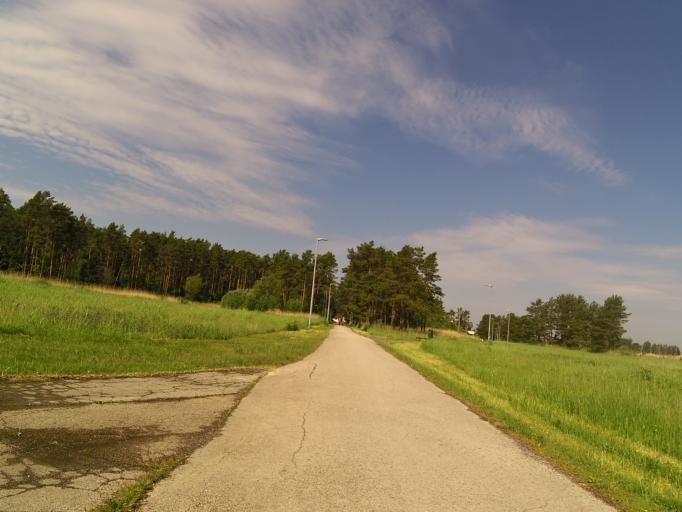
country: EE
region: Laeaene
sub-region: Haapsalu linn
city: Haapsalu
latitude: 58.9392
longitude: 23.5225
